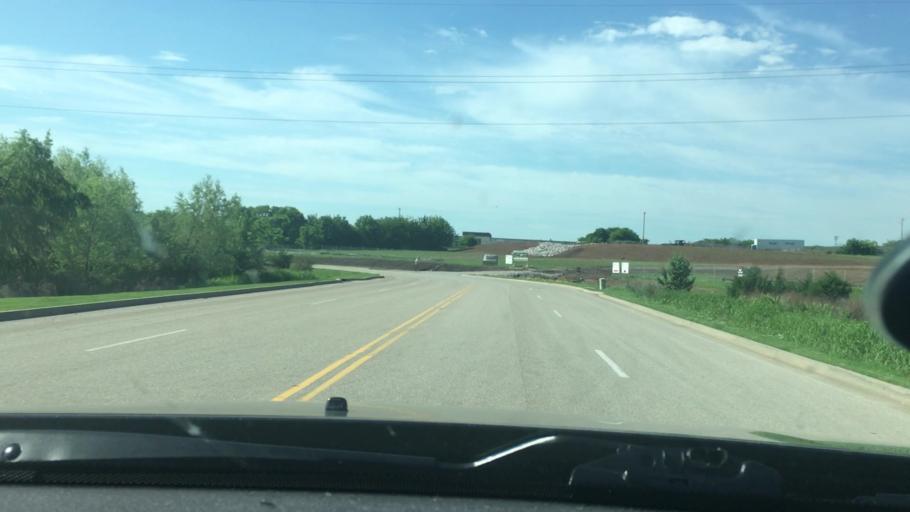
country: US
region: Oklahoma
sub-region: Carter County
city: Ardmore
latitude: 34.2000
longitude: -97.1685
